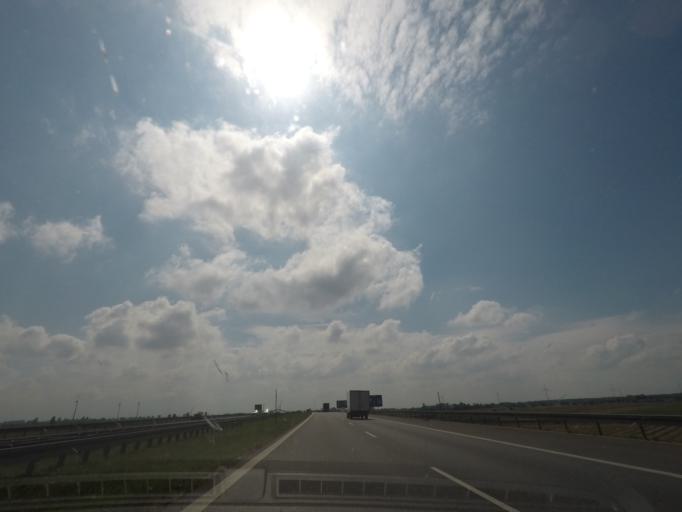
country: PL
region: Lodz Voivodeship
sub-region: Powiat kutnowski
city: Krzyzanow
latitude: 52.2324
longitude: 19.4565
